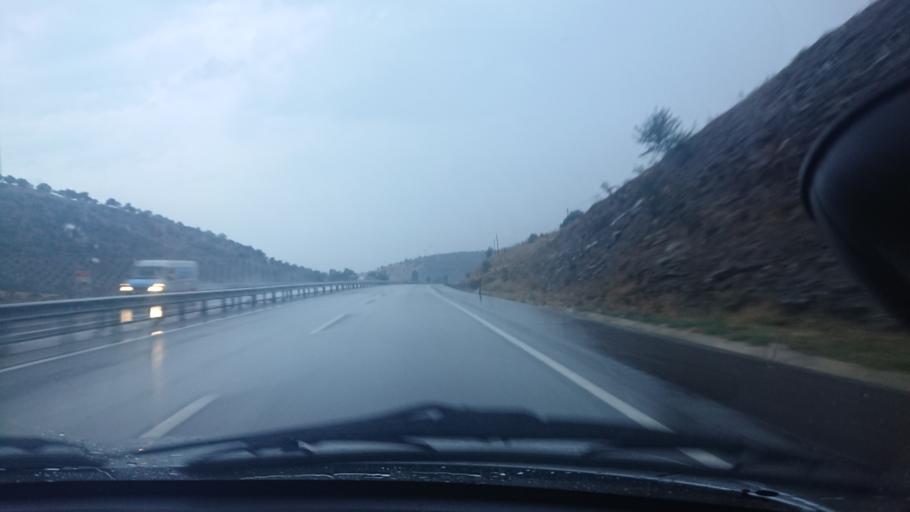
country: TR
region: Manisa
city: Menye
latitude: 38.5435
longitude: 28.4475
